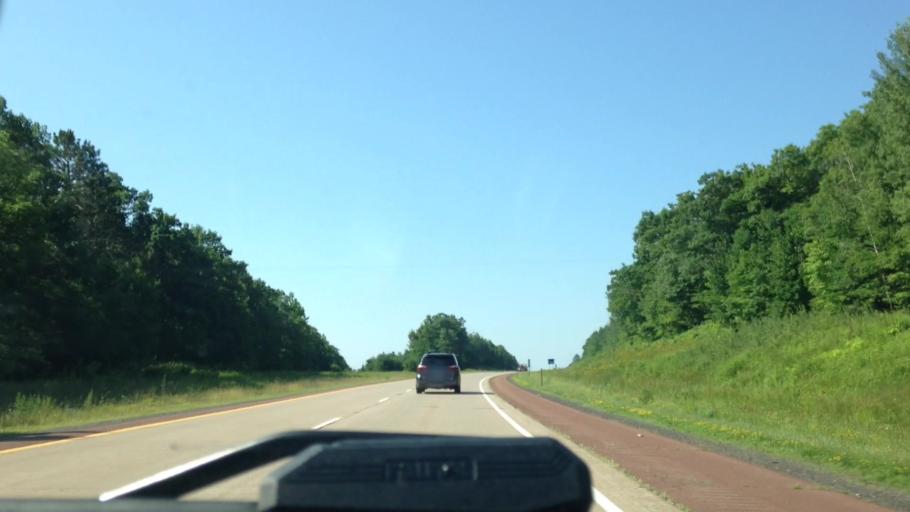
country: US
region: Wisconsin
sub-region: Douglas County
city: Lake Nebagamon
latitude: 46.3896
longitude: -91.8194
